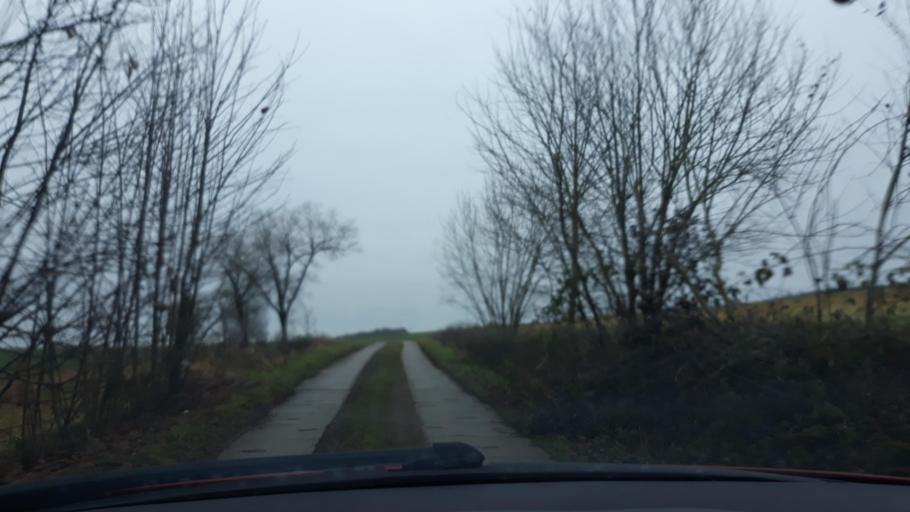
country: DE
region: Saxony
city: Kirchberg
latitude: 50.6468
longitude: 12.5289
